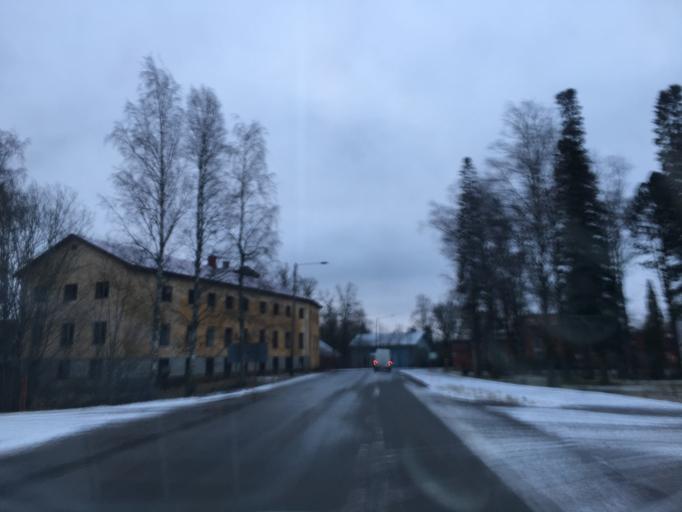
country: FI
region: Varsinais-Suomi
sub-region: Loimaa
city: Aura
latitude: 60.6450
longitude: 22.5913
